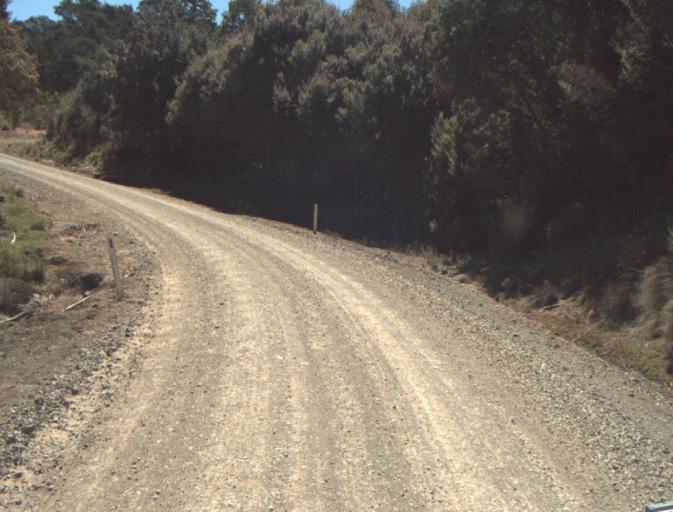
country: AU
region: Tasmania
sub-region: Dorset
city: Scottsdale
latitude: -41.3155
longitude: 147.4650
